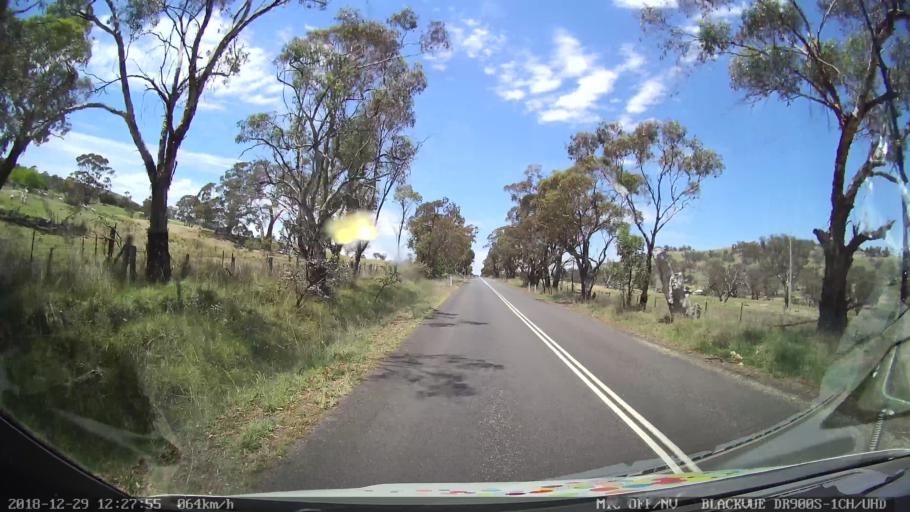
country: AU
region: Australian Capital Territory
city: Macarthur
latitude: -35.4814
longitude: 149.2247
